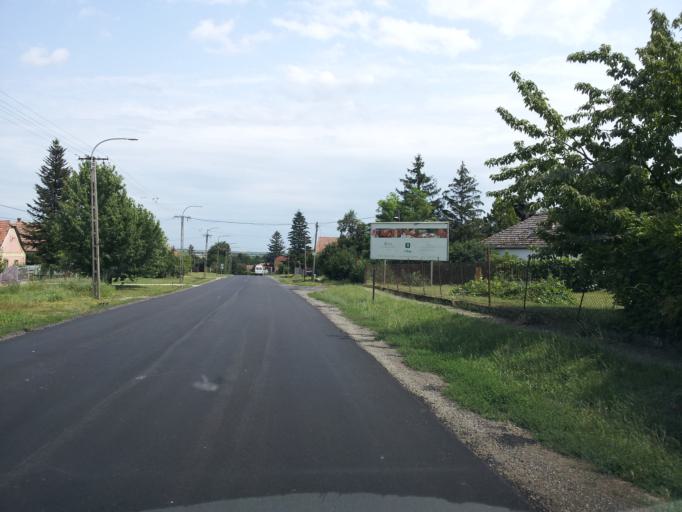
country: HU
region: Fejer
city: Enying
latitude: 46.9551
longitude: 18.2187
